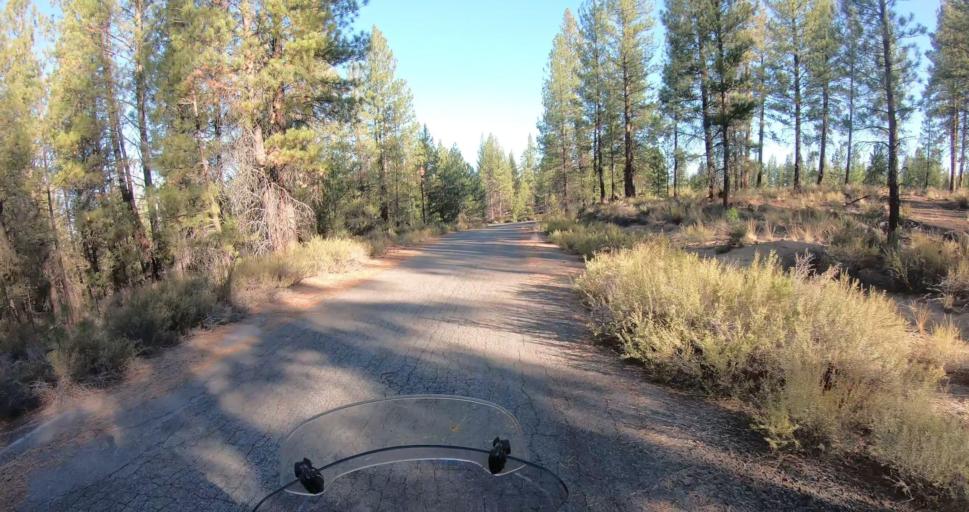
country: US
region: Oregon
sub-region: Deschutes County
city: La Pine
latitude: 43.7192
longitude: -121.4227
